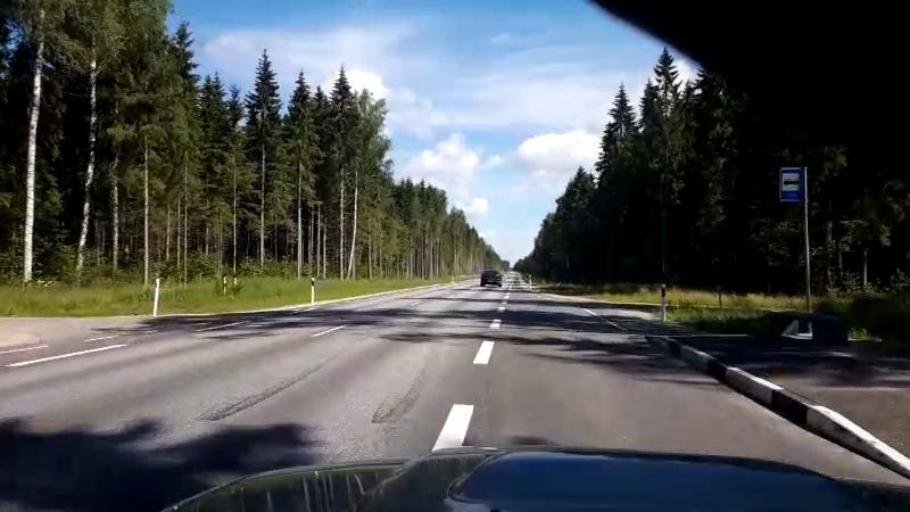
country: EE
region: Jaervamaa
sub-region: Paide linn
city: Paide
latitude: 58.9540
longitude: 25.6516
